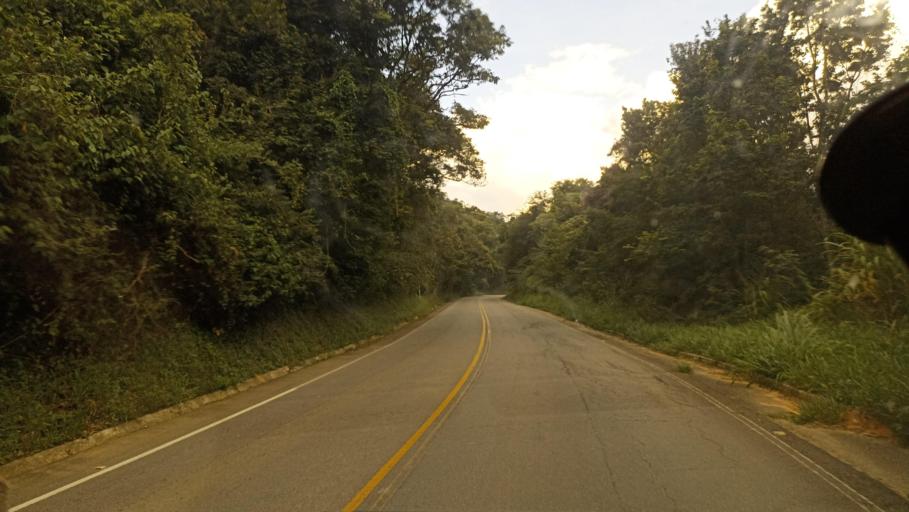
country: BR
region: Minas Gerais
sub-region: Cruzilia
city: Cruzilia
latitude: -21.8724
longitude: -44.8159
